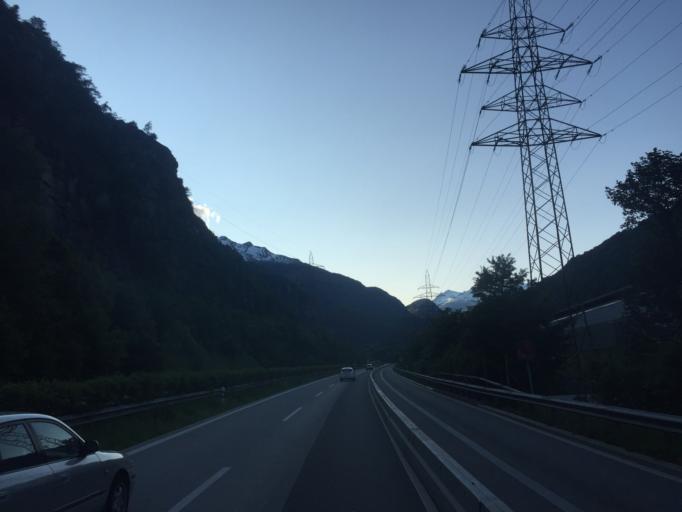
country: CH
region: Ticino
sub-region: Leventina District
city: Bodio
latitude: 46.3839
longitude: 8.8932
